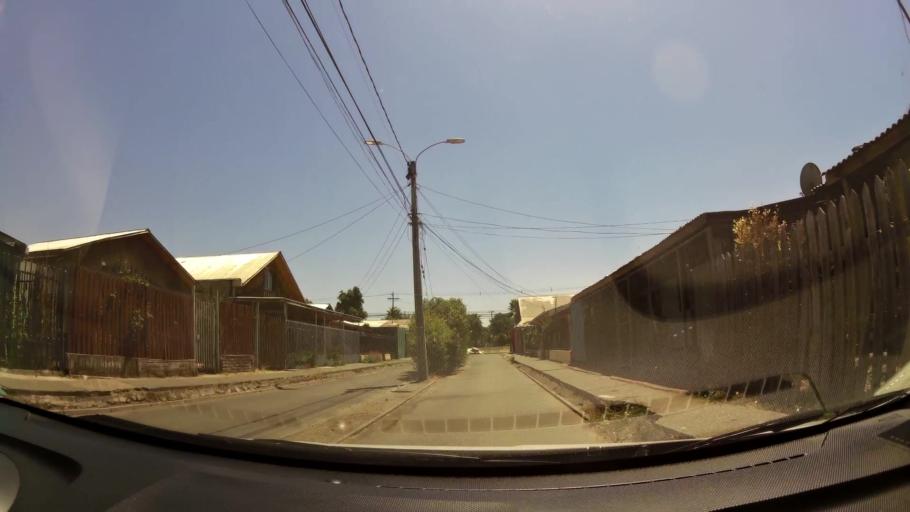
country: CL
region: Maule
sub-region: Provincia de Curico
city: Curico
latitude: -34.9766
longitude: -71.2175
